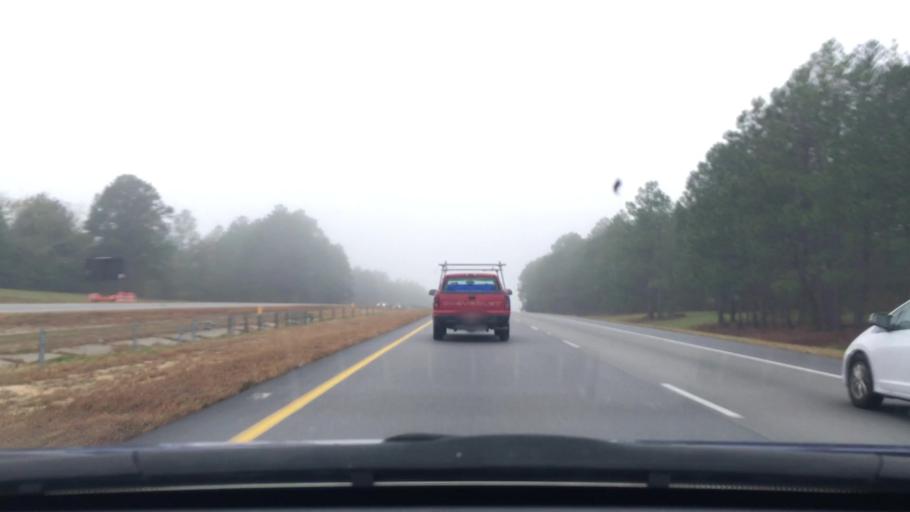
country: US
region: South Carolina
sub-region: Kershaw County
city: Camden
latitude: 34.2099
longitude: -80.4375
